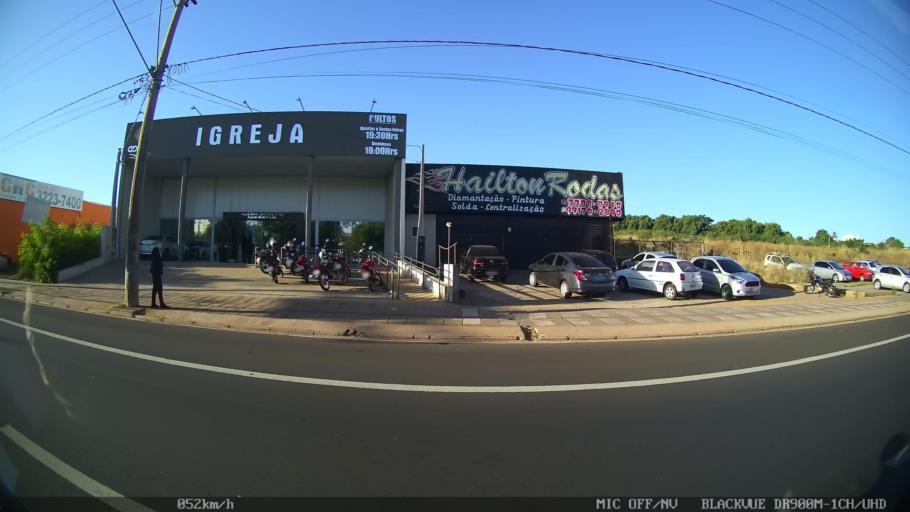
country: BR
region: Sao Paulo
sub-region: Sao Jose Do Rio Preto
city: Sao Jose do Rio Preto
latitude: -20.7846
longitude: -49.3776
